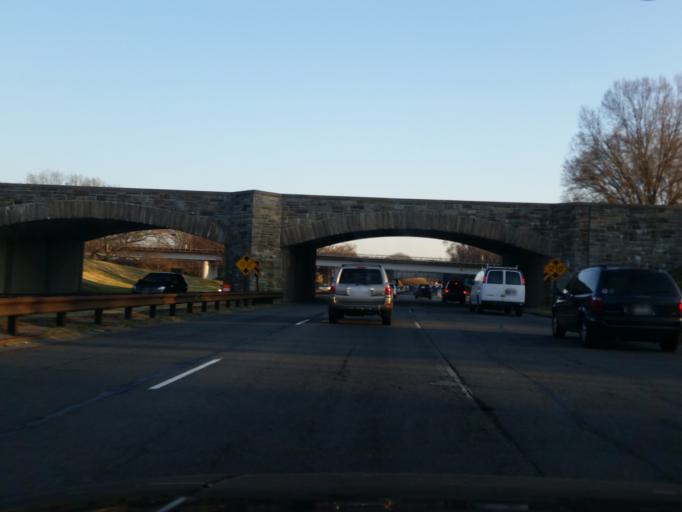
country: US
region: Washington, D.C.
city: Washington, D.C.
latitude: 38.8723
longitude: -77.0436
